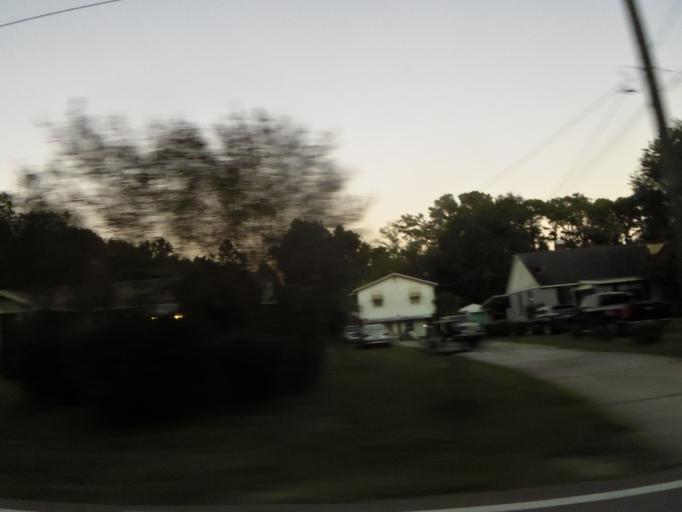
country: US
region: Florida
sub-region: Duval County
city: Jacksonville
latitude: 30.2988
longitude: -81.7220
